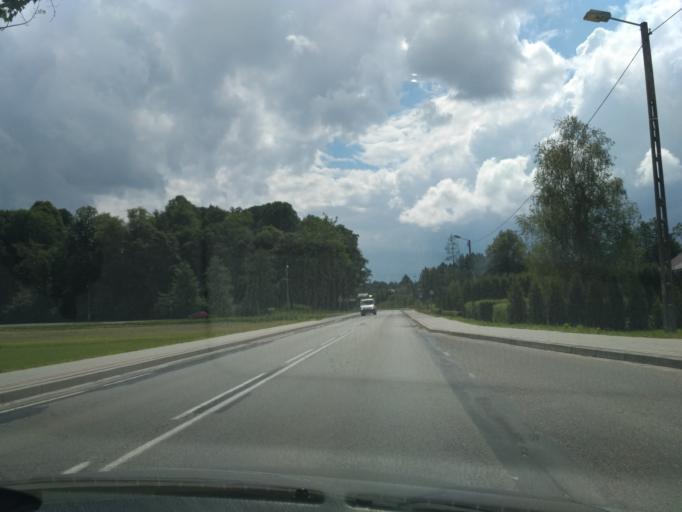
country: PL
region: Subcarpathian Voivodeship
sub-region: Powiat rzeszowski
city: Hyzne
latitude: 49.9240
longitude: 22.1642
